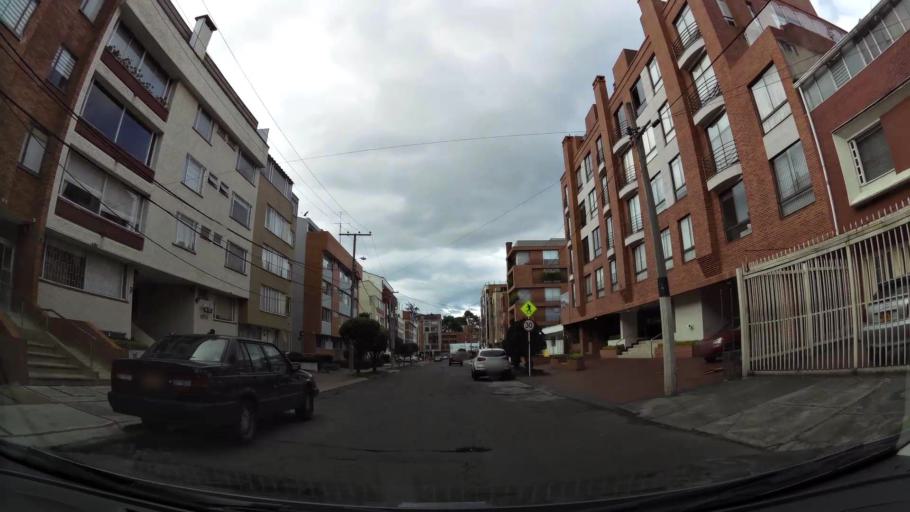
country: CO
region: Bogota D.C.
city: Barrio San Luis
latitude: 4.6942
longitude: -74.0522
